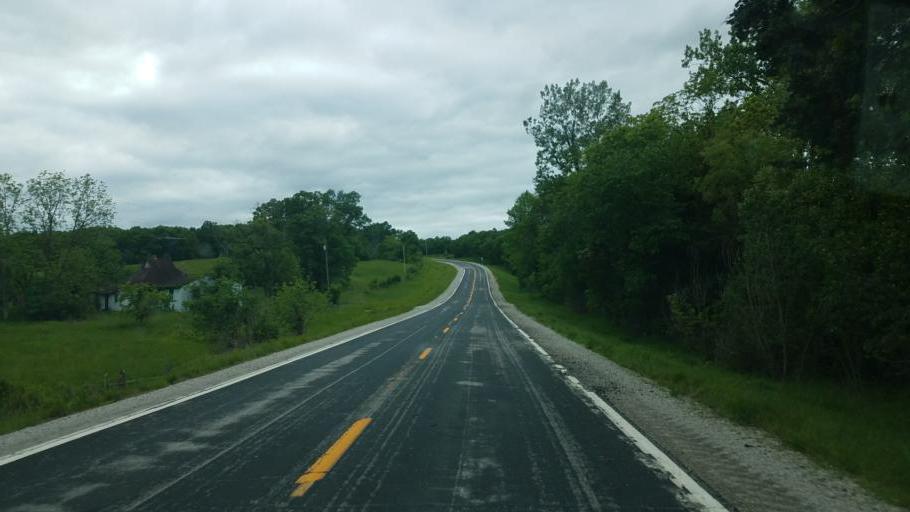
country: US
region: Missouri
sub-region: Mercer County
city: Princeton
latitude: 40.3608
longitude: -93.7394
